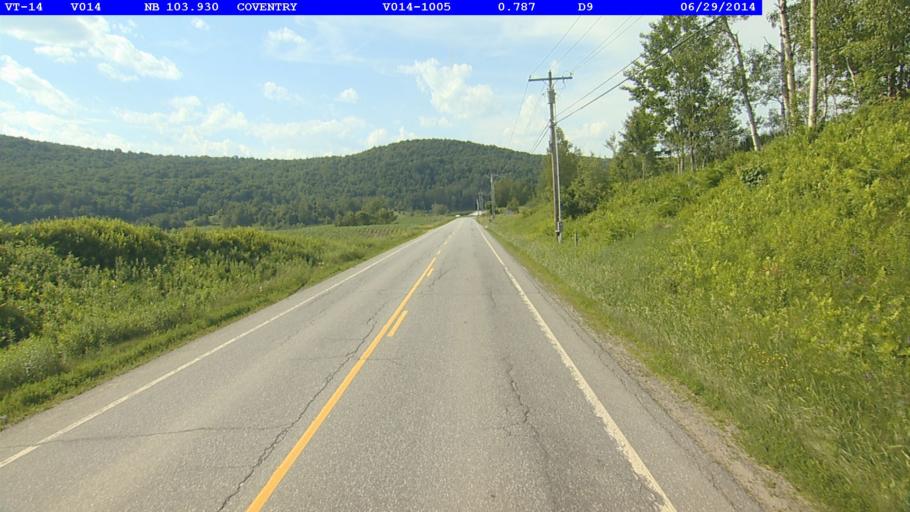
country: US
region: Vermont
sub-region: Orleans County
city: Newport
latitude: 44.8758
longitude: -72.2631
